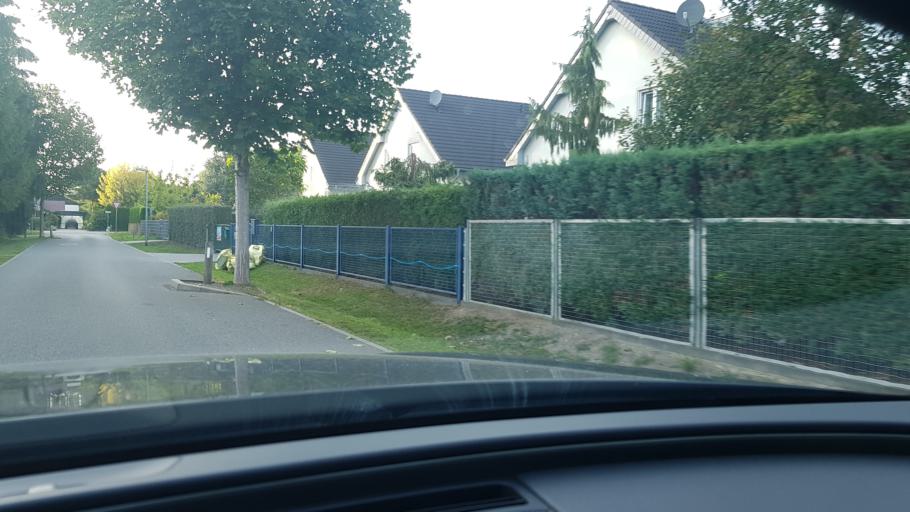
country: DE
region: Brandenburg
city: Brieselang
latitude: 52.5932
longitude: 12.9867
